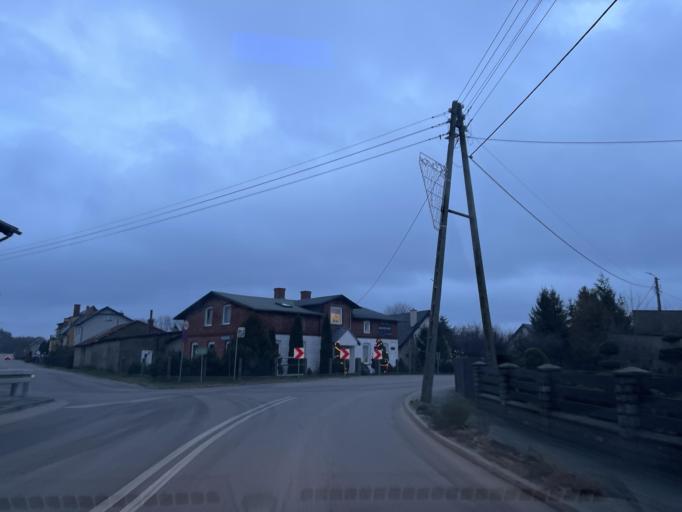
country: PL
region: Pomeranian Voivodeship
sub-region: Powiat wejherowski
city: Szemud
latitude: 54.4149
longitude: 18.2016
